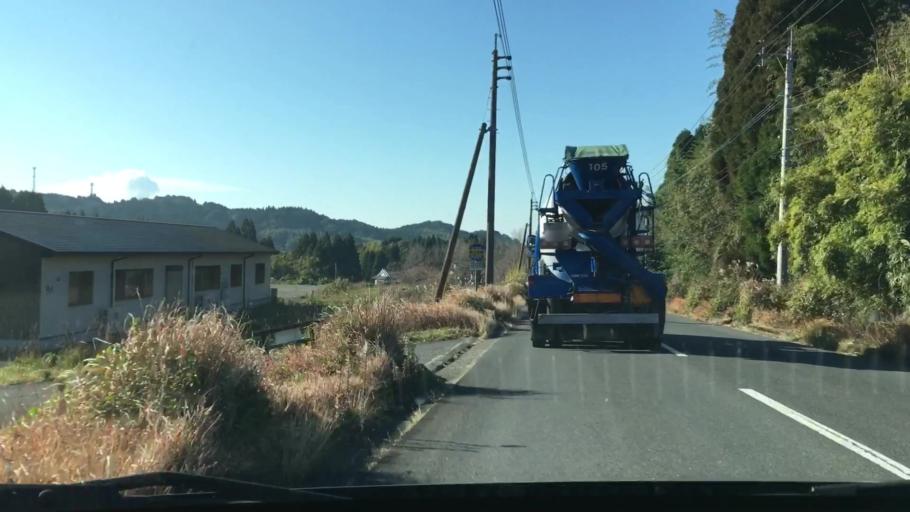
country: JP
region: Kagoshima
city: Kajiki
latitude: 31.7679
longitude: 130.6916
